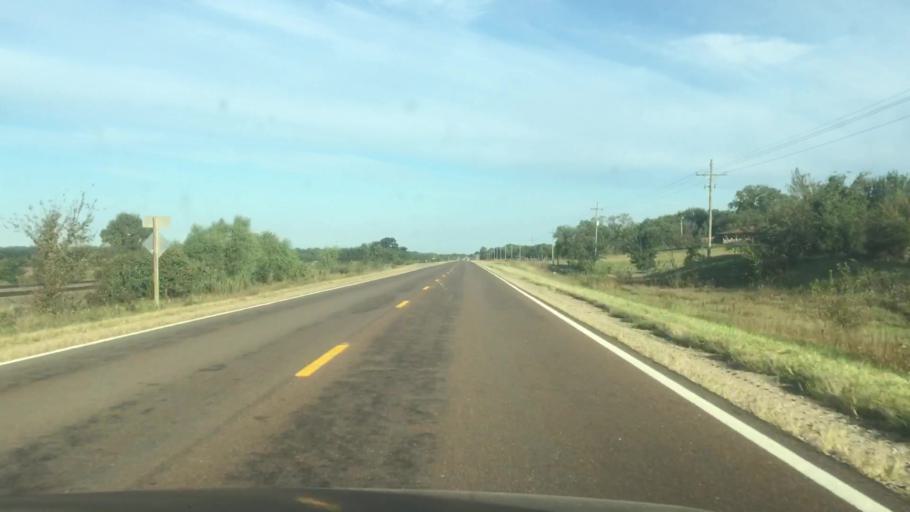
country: US
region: Nebraska
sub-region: Jefferson County
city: Fairbury
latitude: 40.0895
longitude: -97.1221
